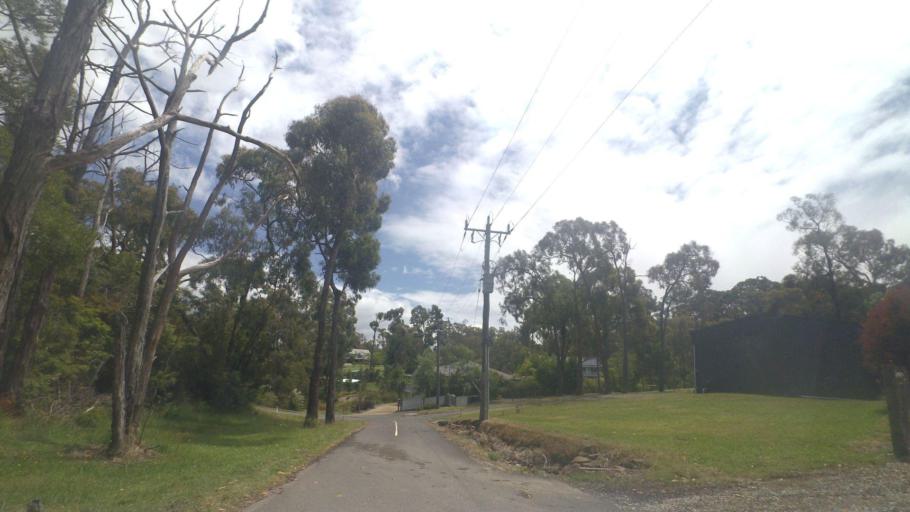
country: AU
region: Victoria
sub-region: Yarra Ranges
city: Mount Evelyn
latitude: -37.7728
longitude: 145.3754
